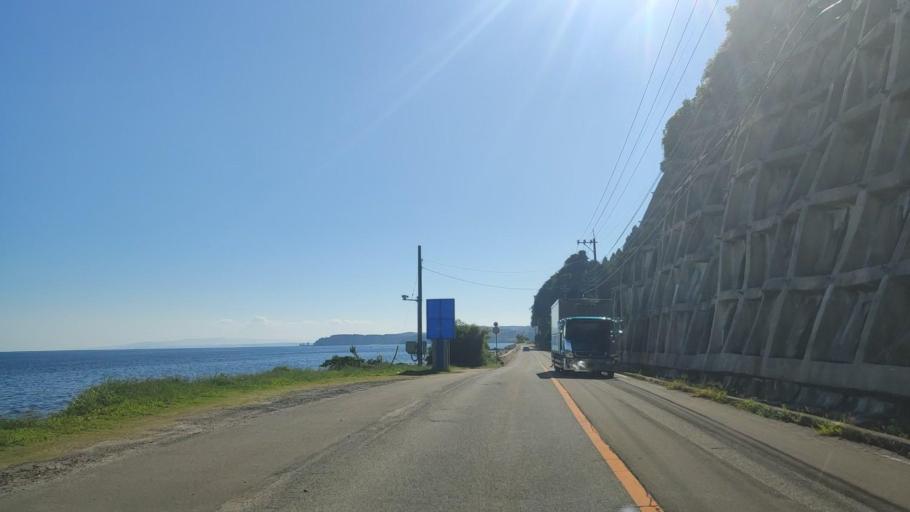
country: JP
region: Ishikawa
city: Nanao
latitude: 37.2836
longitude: 137.1104
